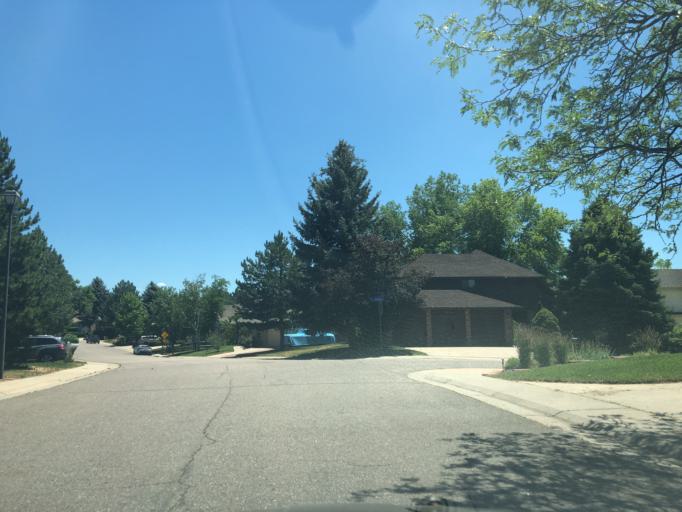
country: US
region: Colorado
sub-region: Arapahoe County
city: Dove Valley
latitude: 39.6163
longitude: -104.7801
